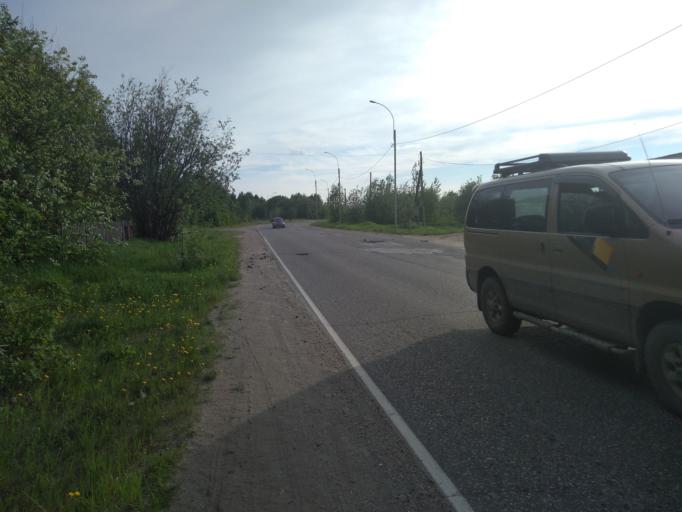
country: RU
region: Komi Republic
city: Pechora
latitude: 65.1464
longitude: 57.2089
